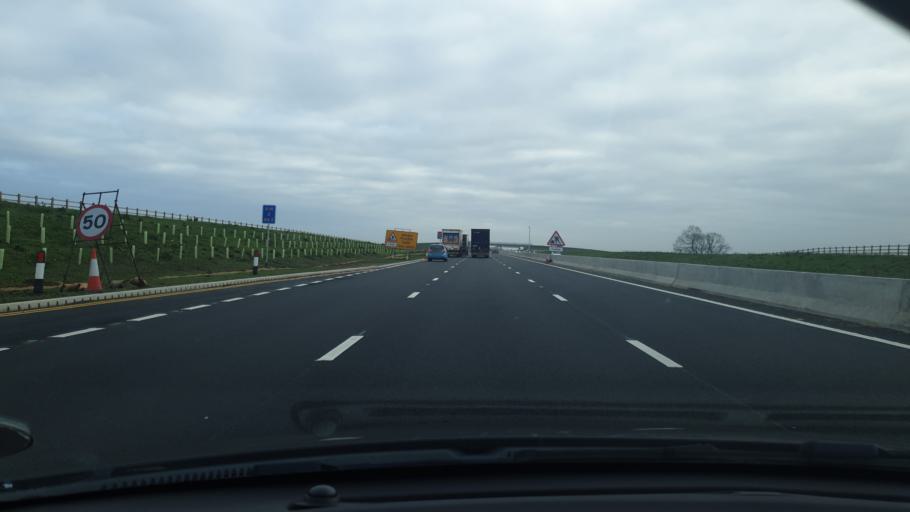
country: GB
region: England
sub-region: Cambridgeshire
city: Needingworth
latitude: 52.2876
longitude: -0.0588
